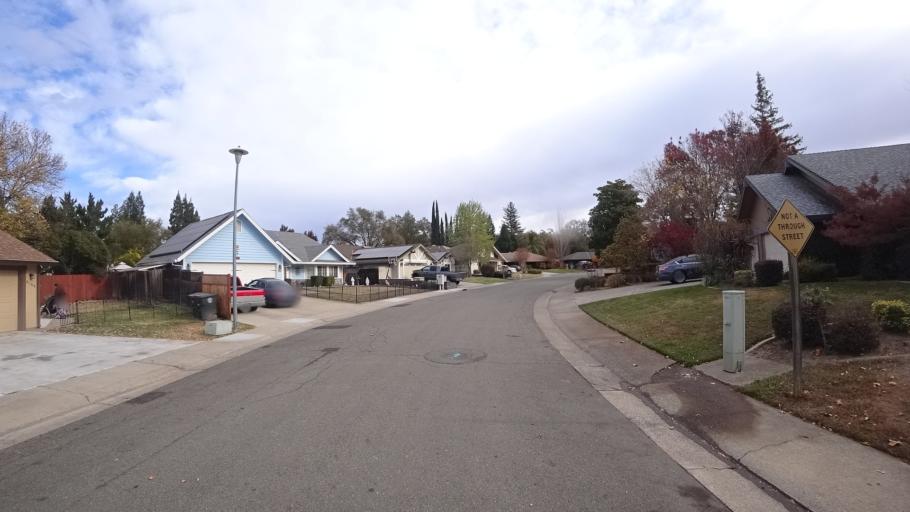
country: US
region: California
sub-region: Sacramento County
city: Citrus Heights
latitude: 38.7149
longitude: -121.2466
